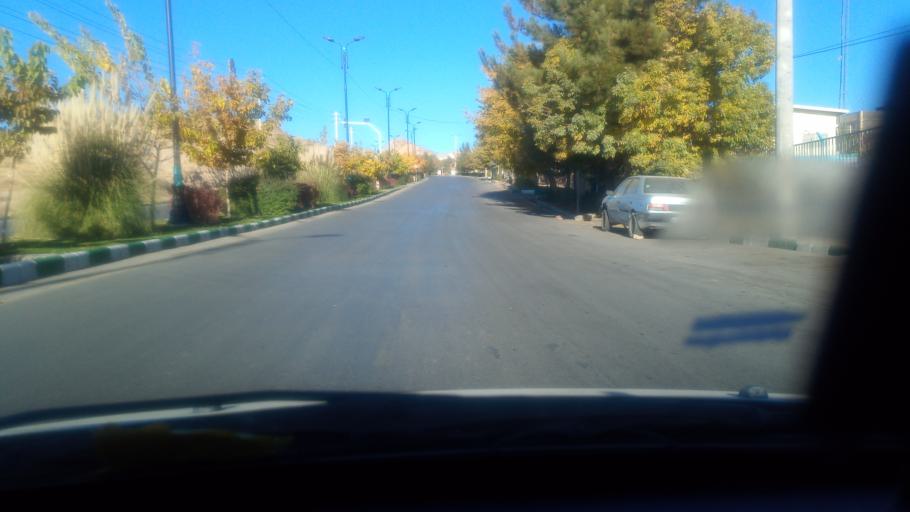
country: IR
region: Razavi Khorasan
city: Torqabeh
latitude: 36.3141
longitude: 59.3659
